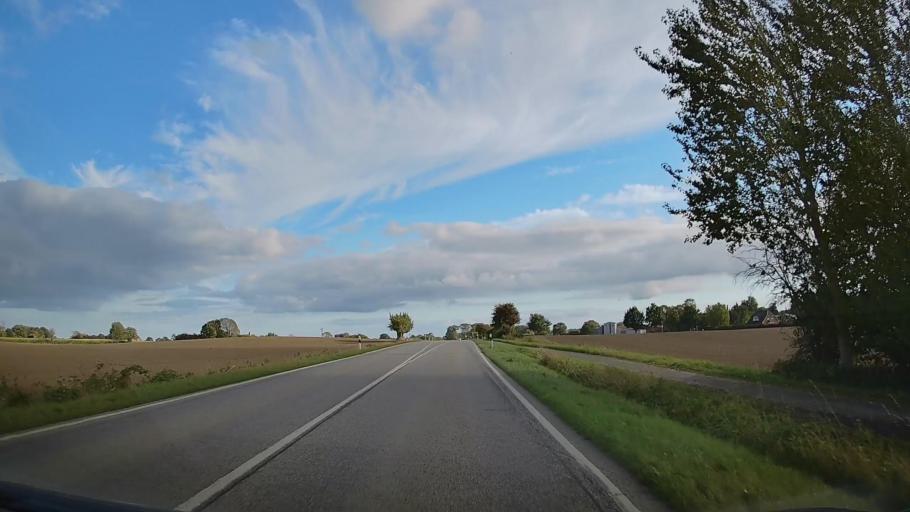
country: DE
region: Schleswig-Holstein
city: Rabel
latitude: 54.7253
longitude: 9.9501
